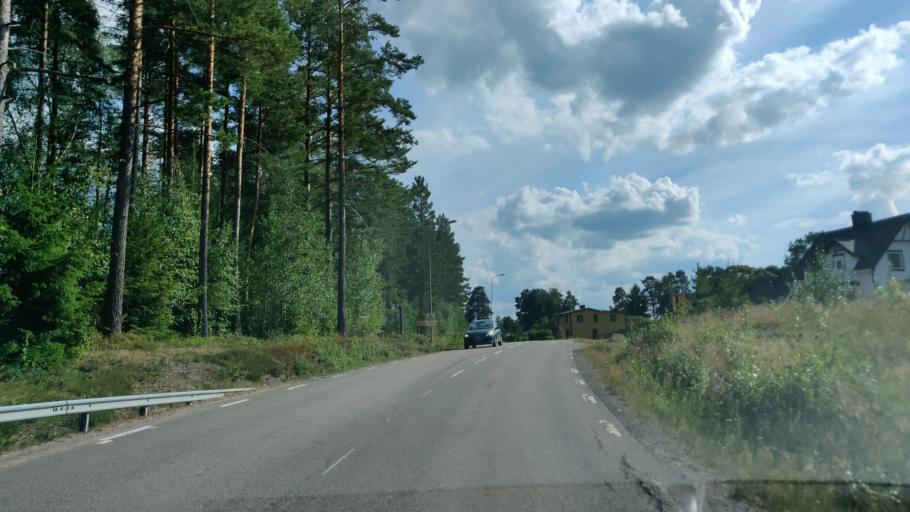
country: SE
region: Vaermland
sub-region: Hagfors Kommun
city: Ekshaerad
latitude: 60.1192
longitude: 13.5631
